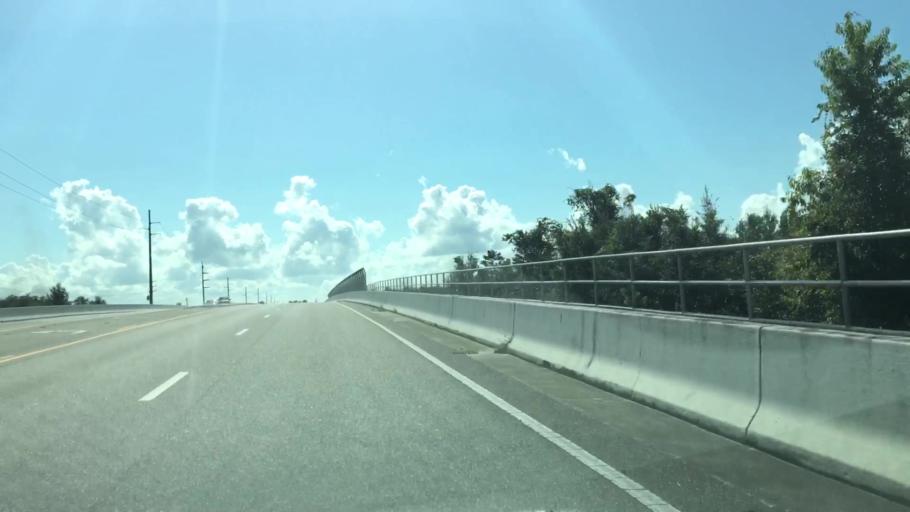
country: US
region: Florida
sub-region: Volusia County
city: Deltona
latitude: 28.8880
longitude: -81.2799
